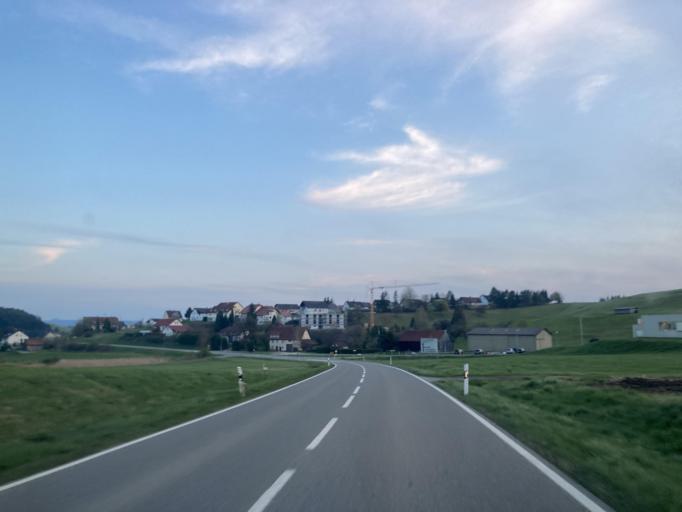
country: DE
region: Baden-Wuerttemberg
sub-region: Freiburg Region
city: Wellendingen
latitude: 48.1548
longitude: 8.7054
